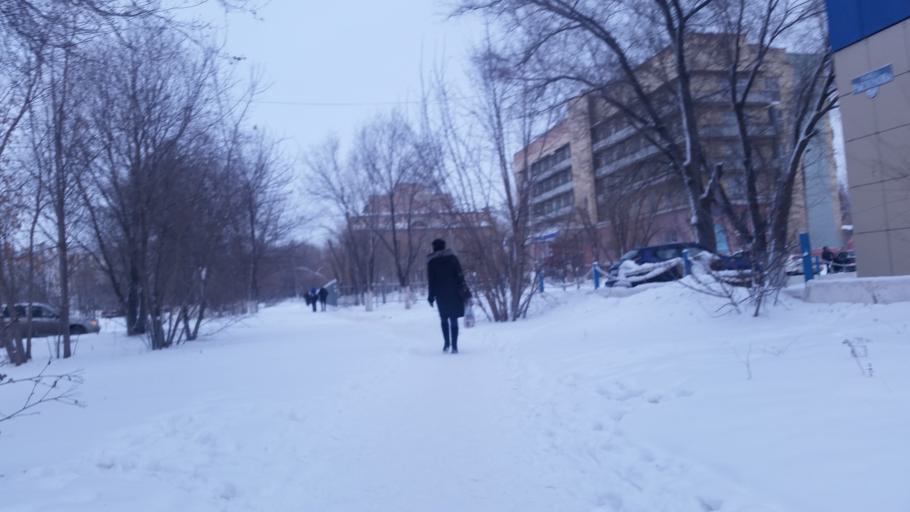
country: KZ
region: Qaraghandy
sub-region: Qaraghandy Qalasy
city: Karagandy
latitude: 49.7689
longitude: 73.1492
